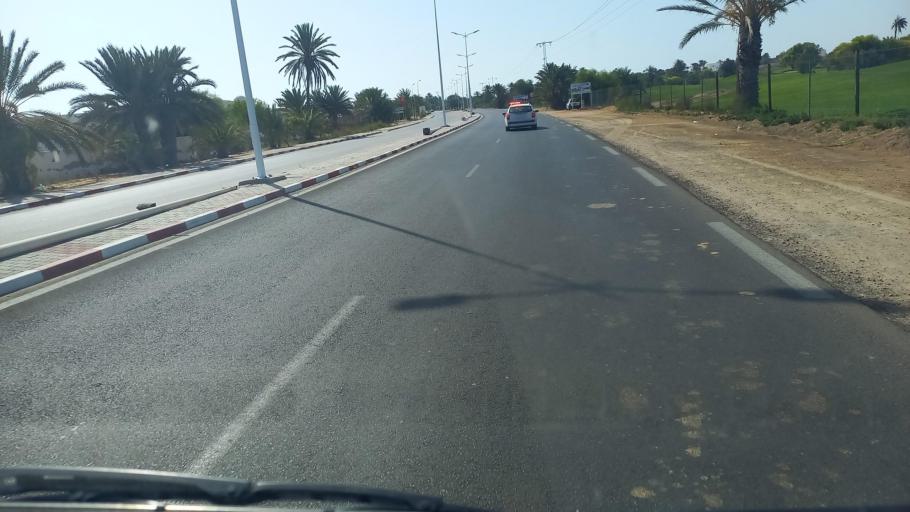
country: TN
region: Madanin
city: Midoun
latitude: 33.8336
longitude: 11.0035
